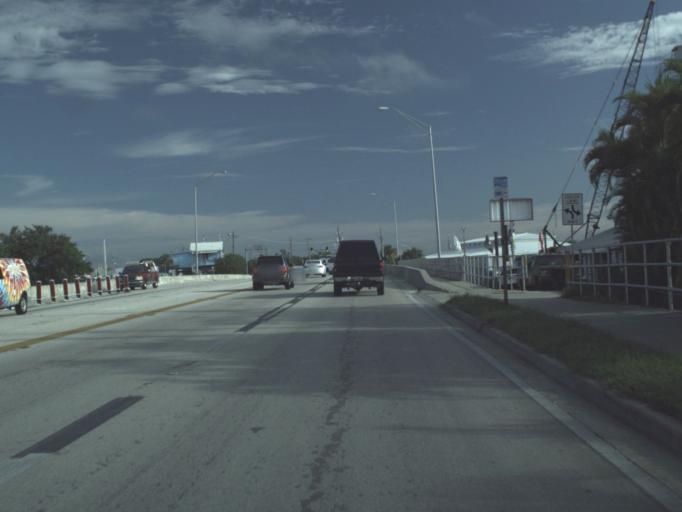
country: US
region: Florida
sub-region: Lee County
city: Fort Myers Beach
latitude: 26.4655
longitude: -81.9514
